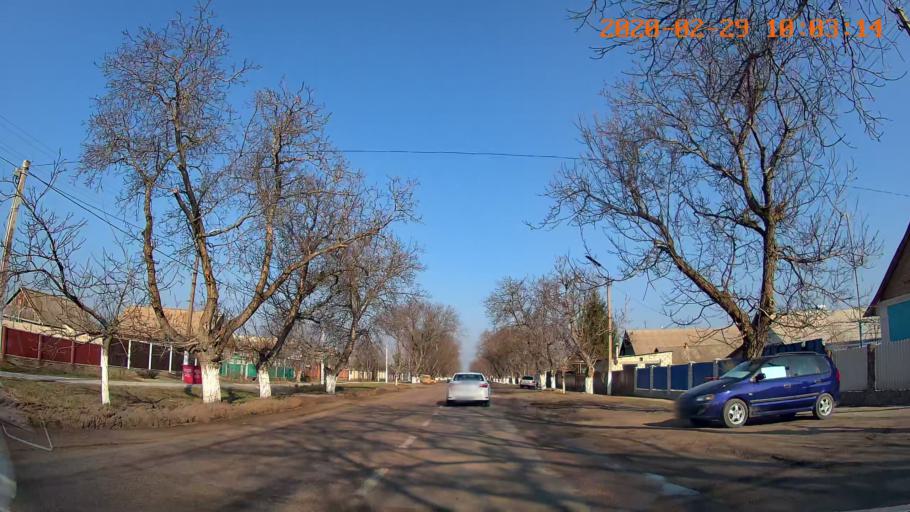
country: MD
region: Telenesti
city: Slobozia
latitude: 46.7892
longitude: 29.6810
